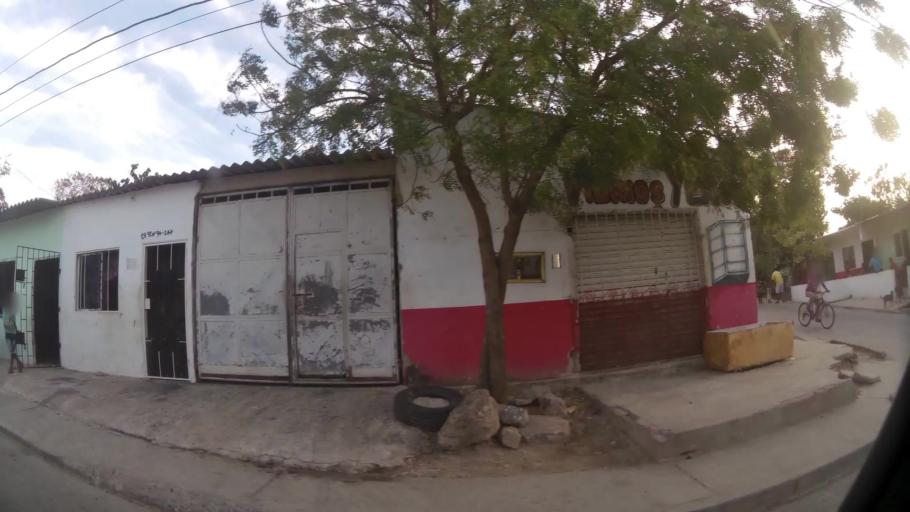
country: CO
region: Atlantico
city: Barranquilla
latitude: 10.9563
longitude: -74.8281
